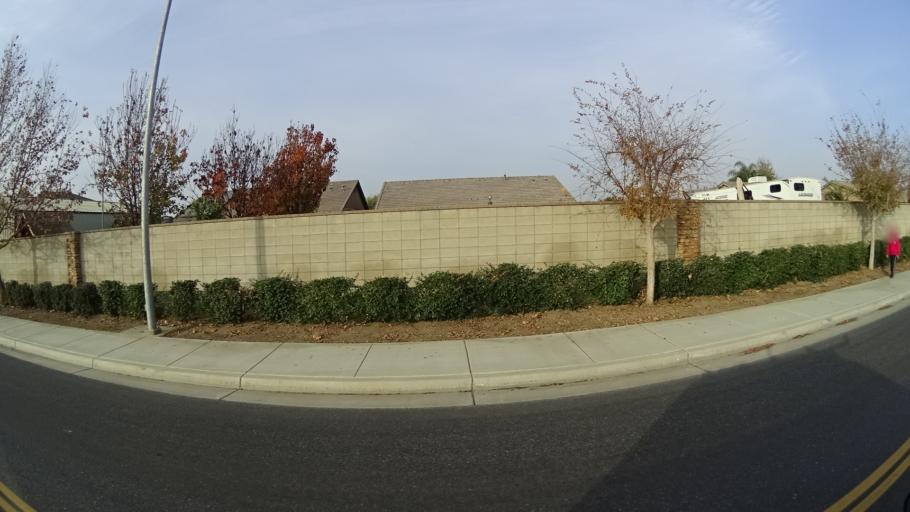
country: US
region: California
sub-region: Kern County
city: Greenacres
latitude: 35.4298
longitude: -119.1190
